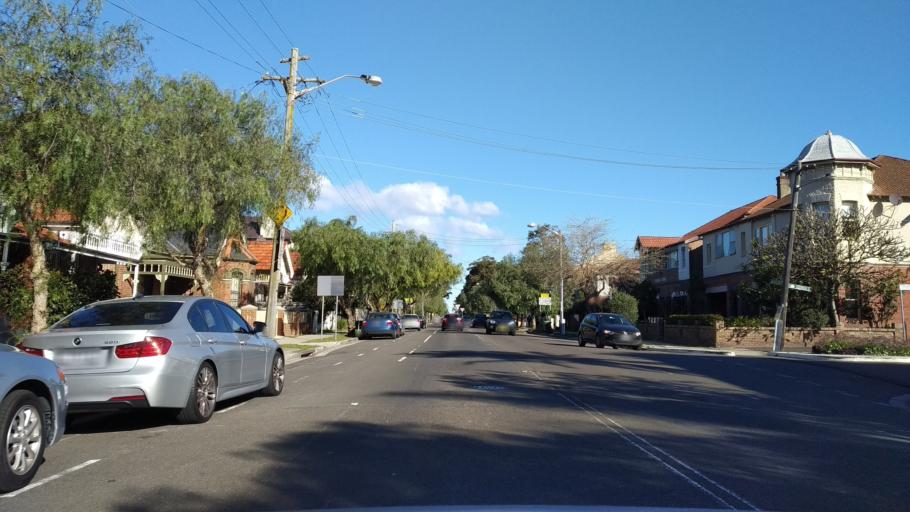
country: AU
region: New South Wales
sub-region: Randwick
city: Kensington
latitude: -33.9071
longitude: 151.2259
